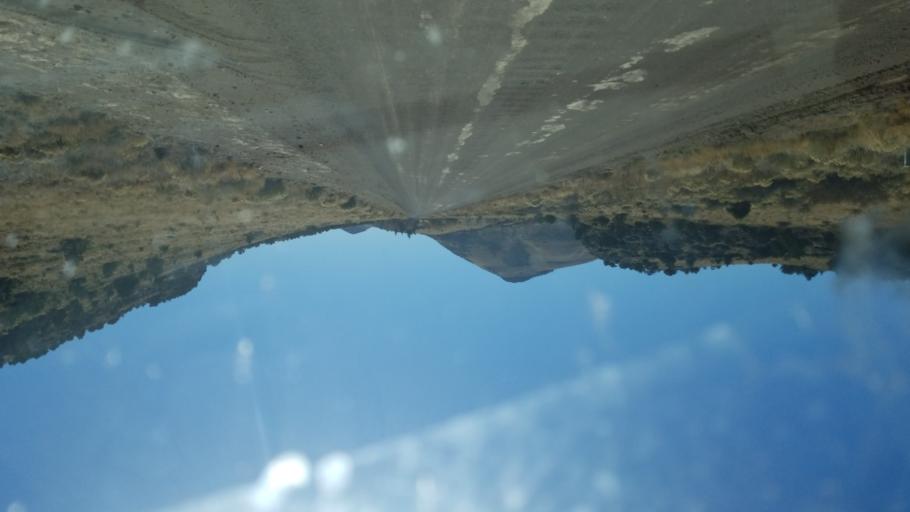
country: US
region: Colorado
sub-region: Rio Grande County
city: Del Norte
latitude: 37.6344
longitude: -106.3653
